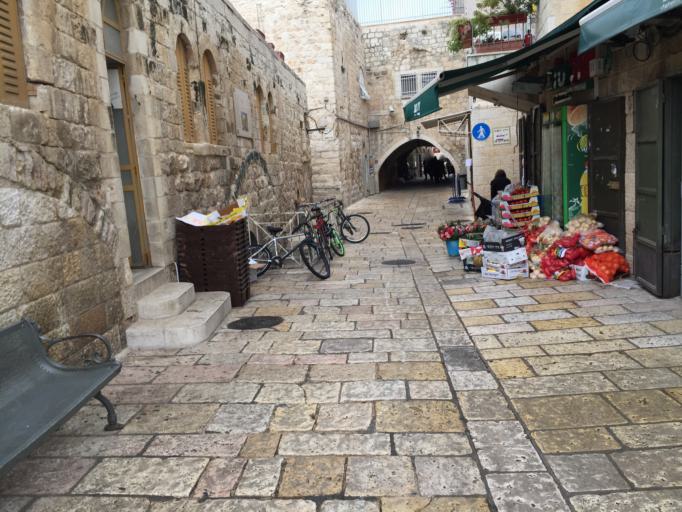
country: PS
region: West Bank
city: Old City
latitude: 31.7742
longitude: 35.2310
